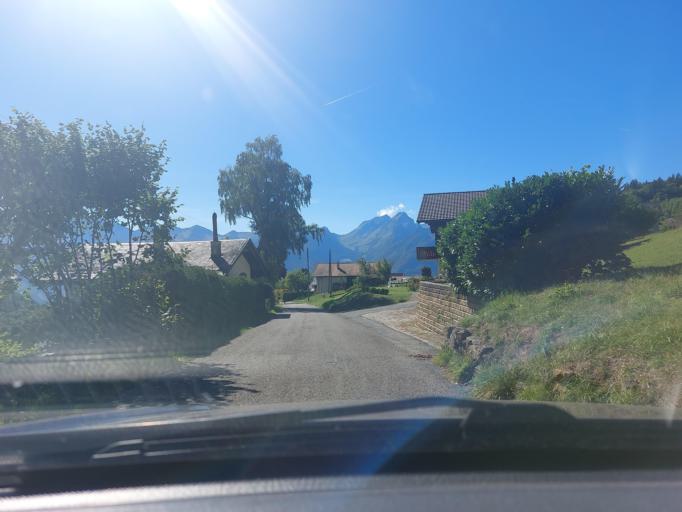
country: CH
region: Vaud
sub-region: Aigle District
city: Aigle
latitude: 46.3513
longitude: 6.9624
